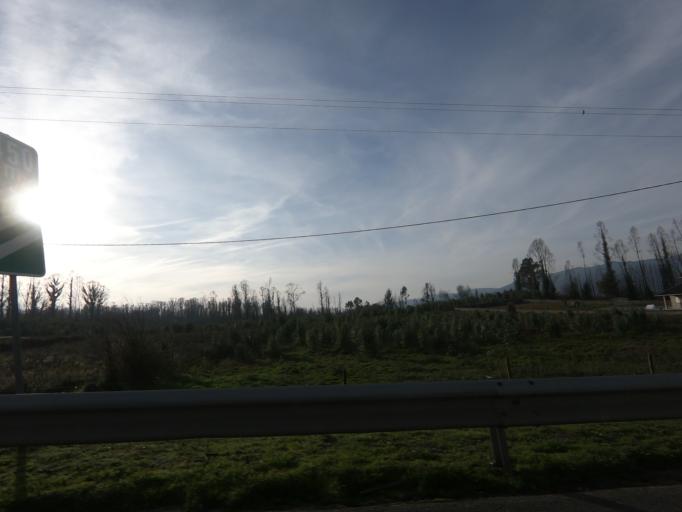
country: PT
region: Viseu
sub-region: Concelho de Tondela
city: Tondela
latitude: 40.5065
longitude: -8.0850
